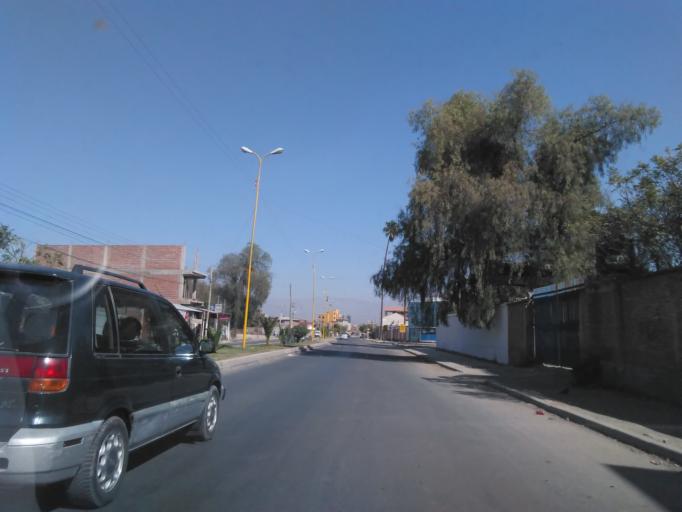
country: BO
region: Cochabamba
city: Cochabamba
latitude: -17.3940
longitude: -66.2694
